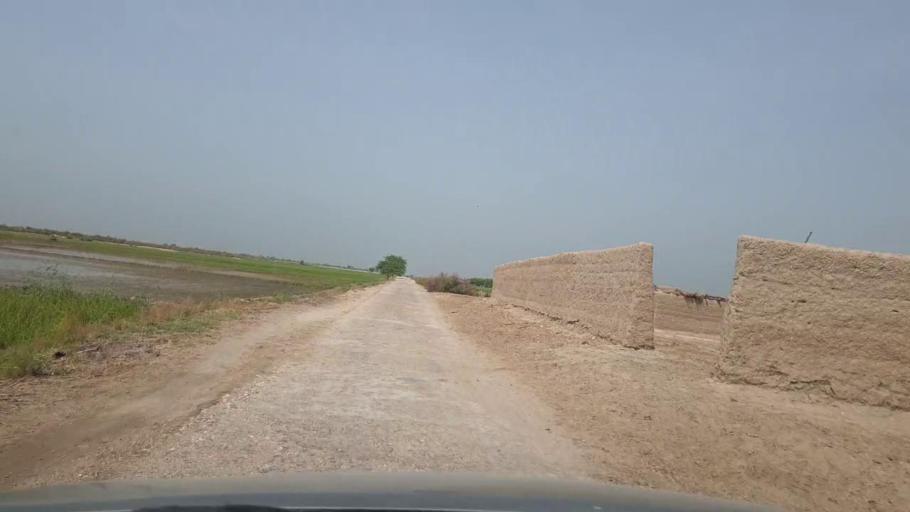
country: PK
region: Sindh
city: Garhi Yasin
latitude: 27.9170
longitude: 68.4286
